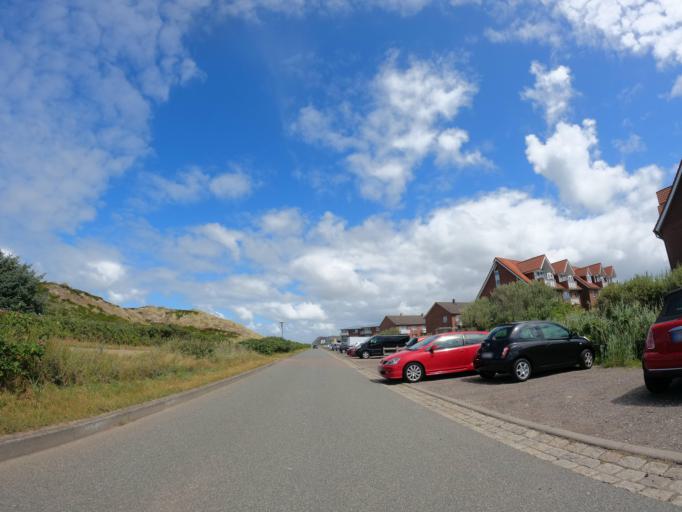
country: DE
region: Schleswig-Holstein
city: Westerland
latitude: 54.8575
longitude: 8.2909
